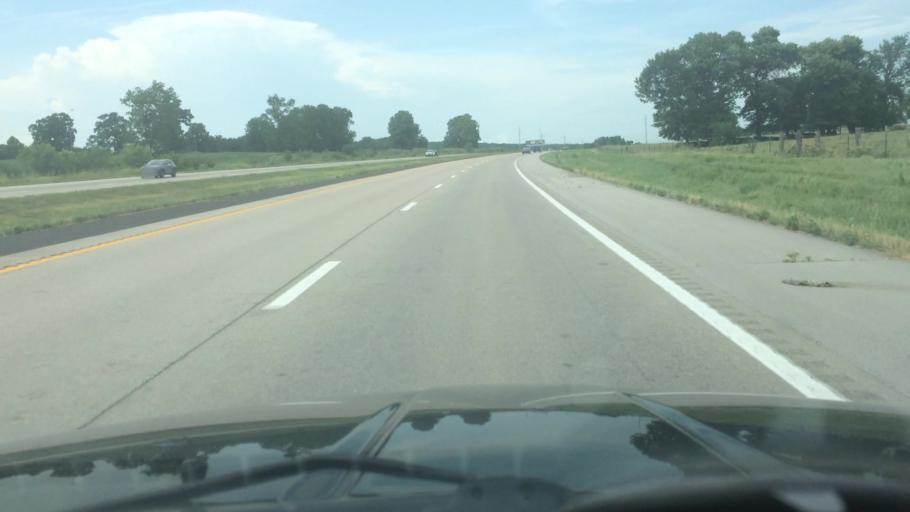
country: US
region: Missouri
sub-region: Polk County
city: Humansville
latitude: 37.8235
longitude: -93.6162
